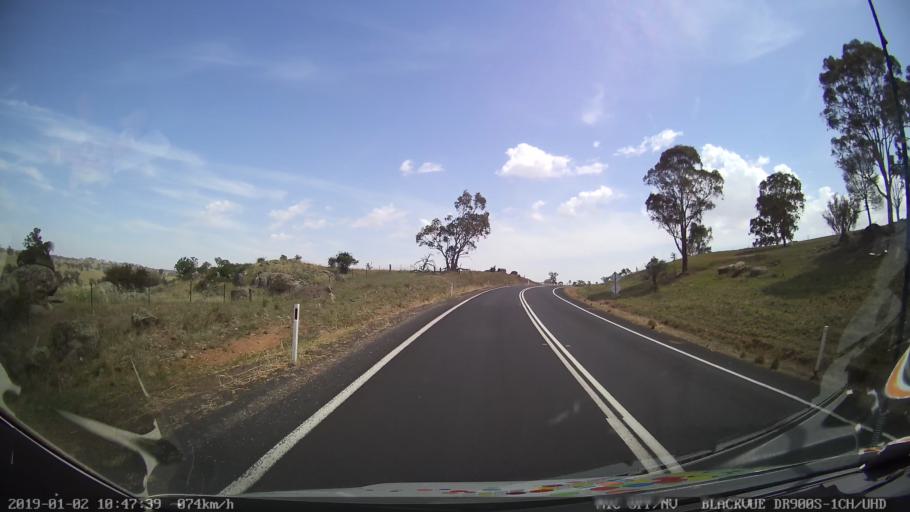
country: AU
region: New South Wales
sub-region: Cootamundra
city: Cootamundra
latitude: -34.7428
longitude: 148.2717
